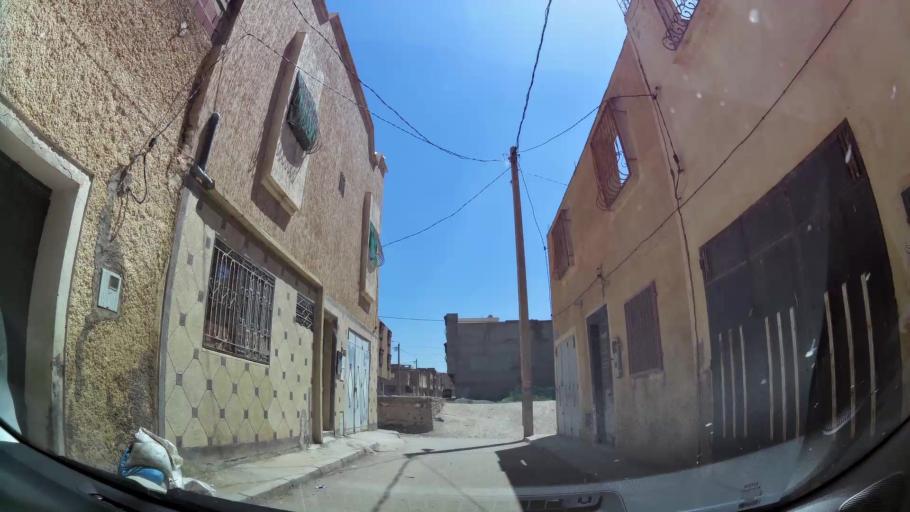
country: MA
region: Oriental
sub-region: Oujda-Angad
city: Oujda
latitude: 34.6907
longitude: -1.9420
